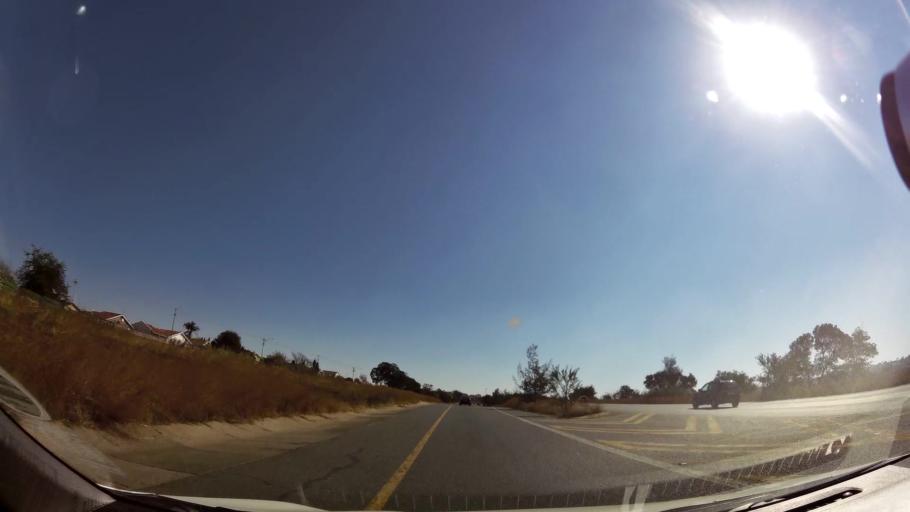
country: ZA
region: Gauteng
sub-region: City of Johannesburg Metropolitan Municipality
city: Johannesburg
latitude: -26.2737
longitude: 28.0334
